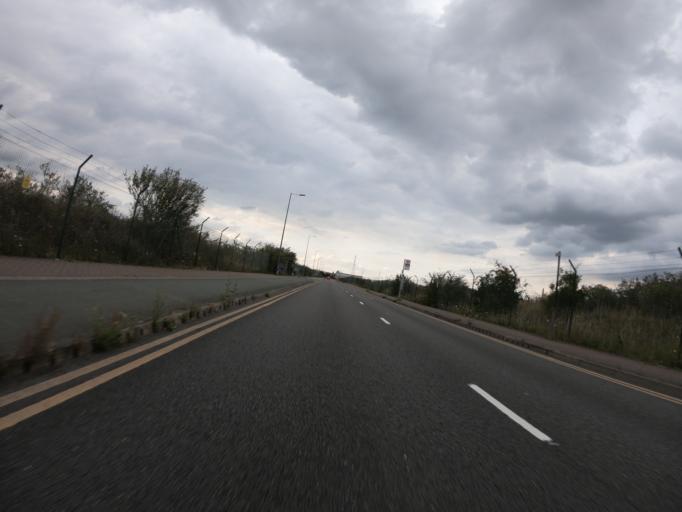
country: GB
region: England
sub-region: Greater London
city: Barking
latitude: 51.5118
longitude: 0.0807
